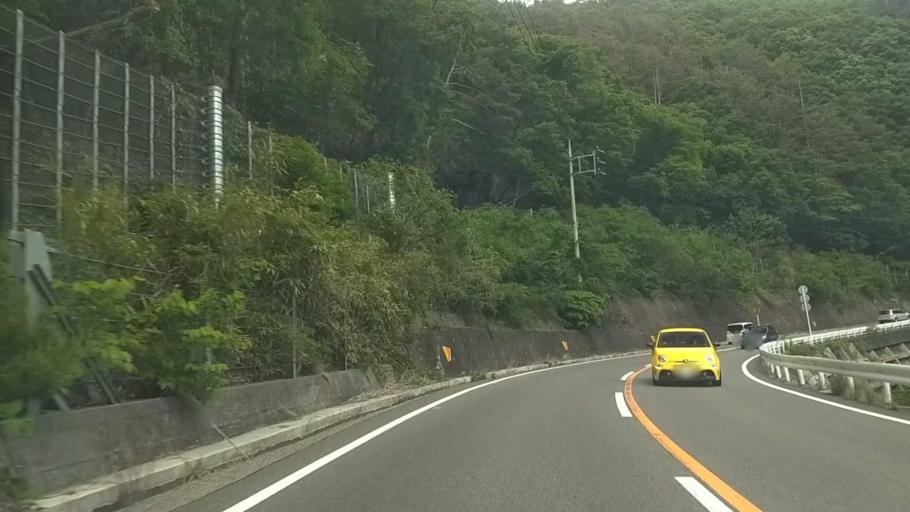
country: JP
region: Yamanashi
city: Fujikawaguchiko
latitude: 35.5313
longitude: 138.6224
